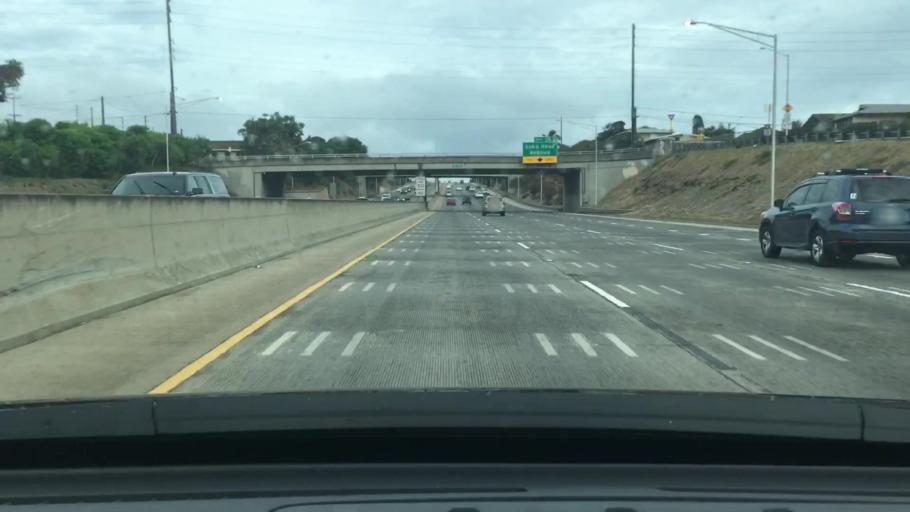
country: US
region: Hawaii
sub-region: Honolulu County
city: Honolulu
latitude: 21.2843
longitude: -157.8082
